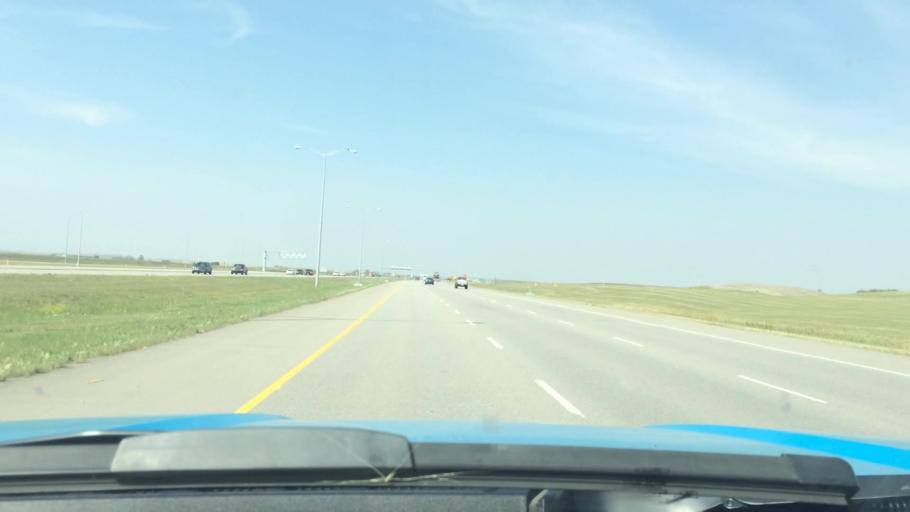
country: CA
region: Alberta
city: Chestermere
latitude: 50.9817
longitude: -113.9204
